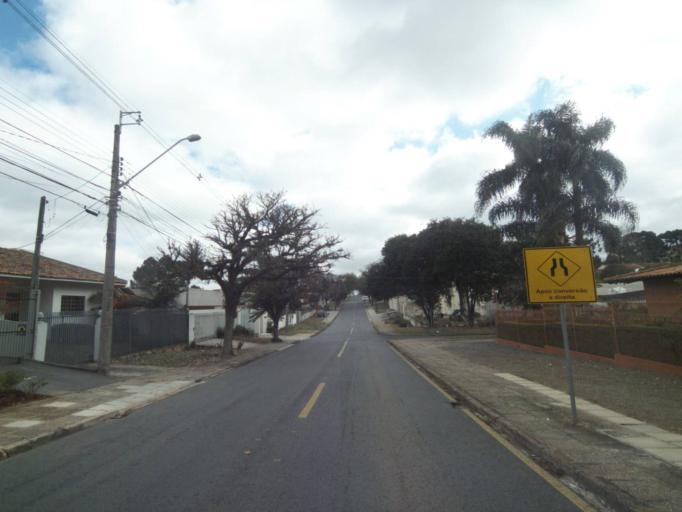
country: BR
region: Parana
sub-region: Curitiba
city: Curitiba
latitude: -25.4477
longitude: -49.3024
